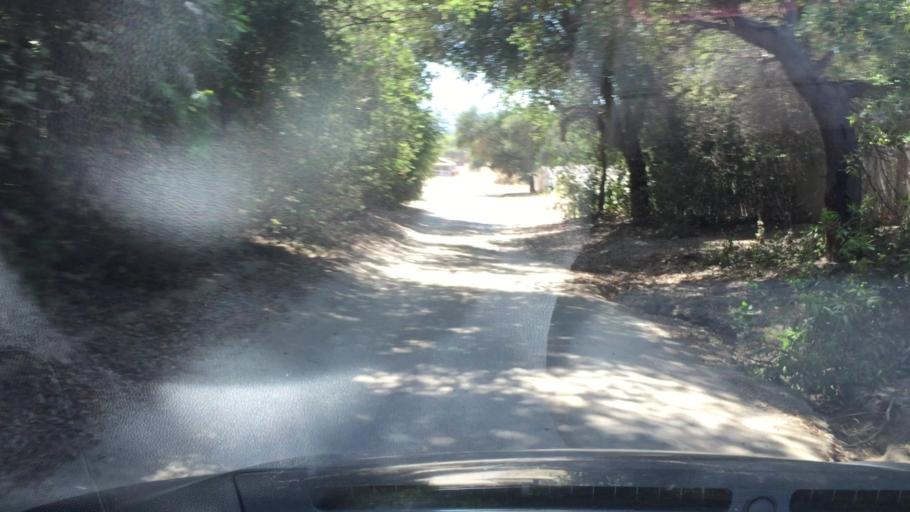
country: US
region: California
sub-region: San Diego County
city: Alpine
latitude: 32.7538
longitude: -116.7539
